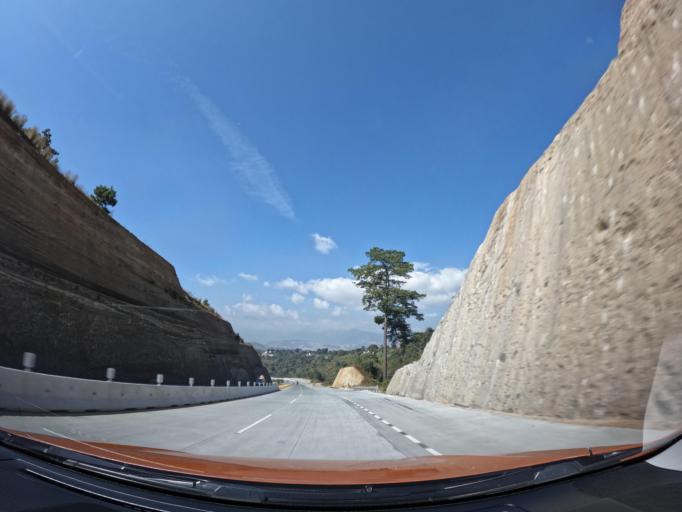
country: GT
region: Guatemala
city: Villa Canales
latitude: 14.4938
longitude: -90.5180
